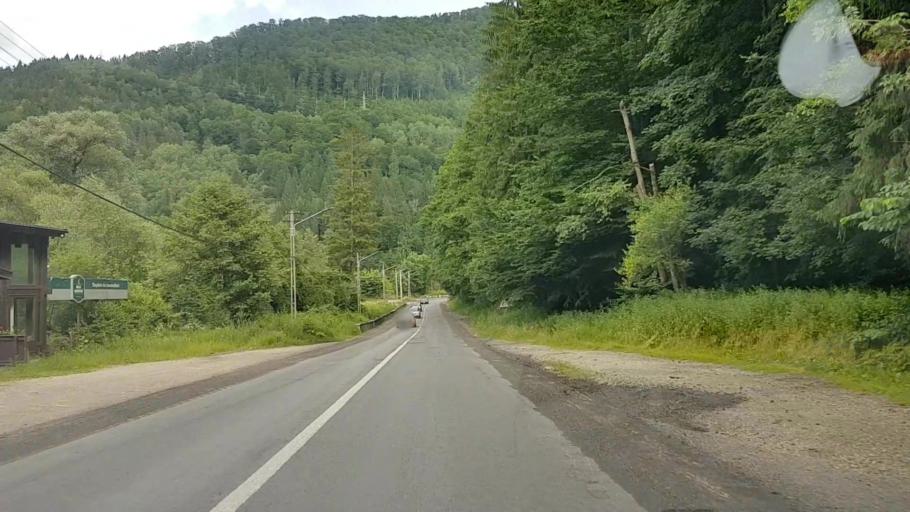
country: RO
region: Neamt
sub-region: Comuna Bicaz
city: Dodeni
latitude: 46.9355
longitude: 26.0954
